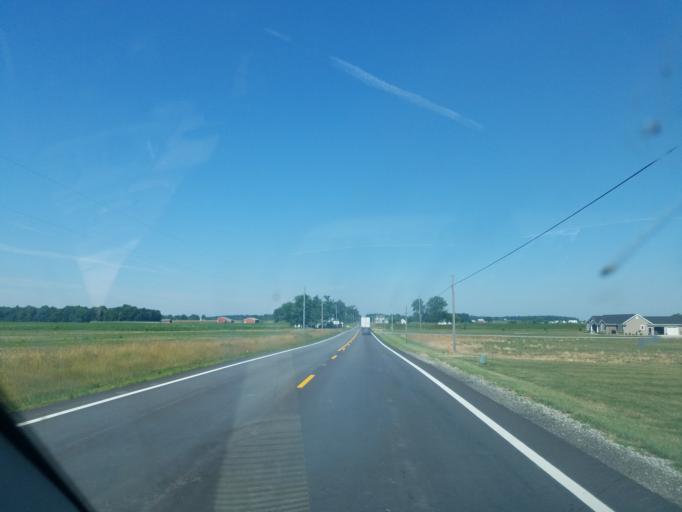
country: US
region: Ohio
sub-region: Shelby County
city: Jackson Center
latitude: 40.4396
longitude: -84.0759
